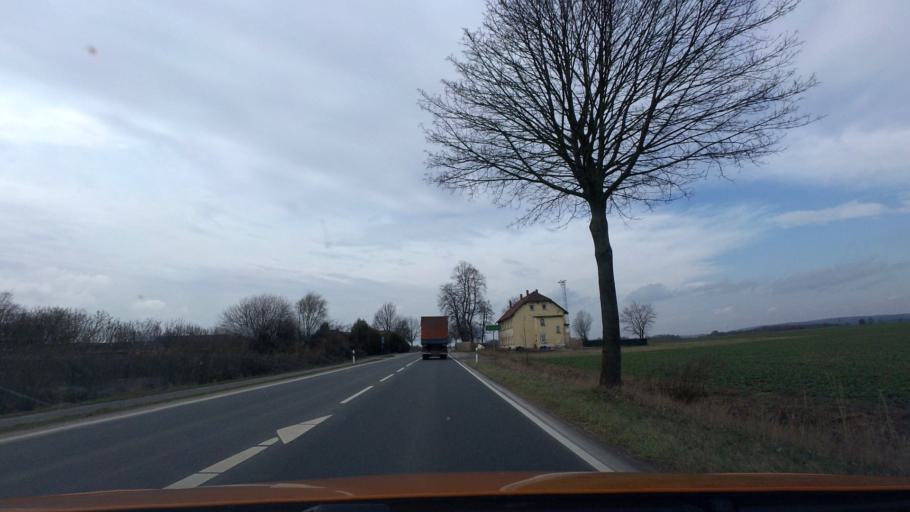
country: DE
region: Lower Saxony
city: Frellstedt
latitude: 52.2252
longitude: 10.9281
